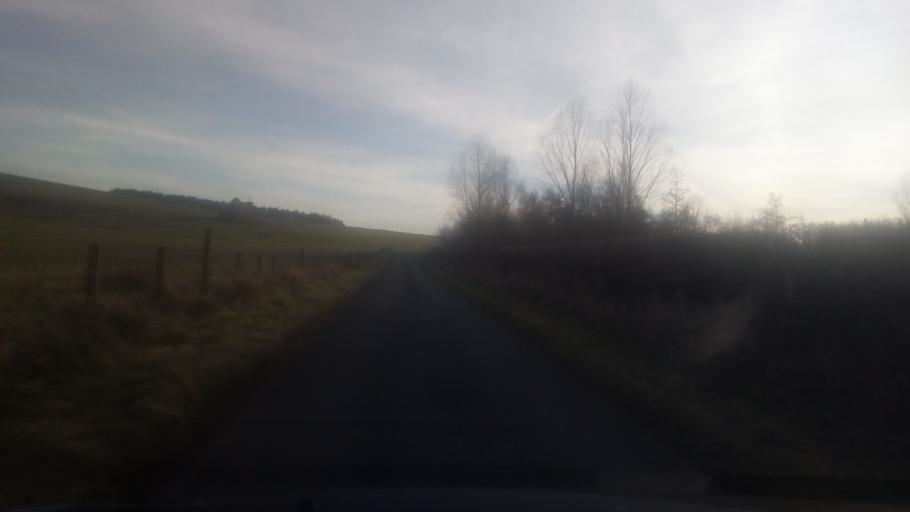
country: GB
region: Scotland
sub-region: The Scottish Borders
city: Jedburgh
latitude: 55.4363
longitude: -2.6253
